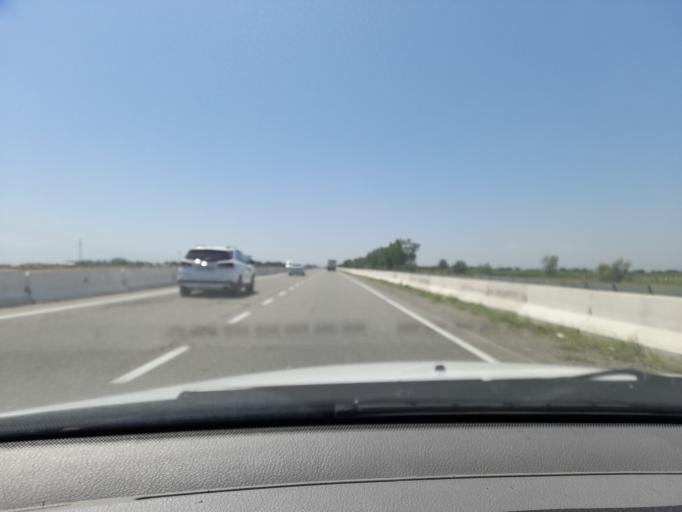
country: UZ
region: Jizzax
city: Paxtakor
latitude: 40.3378
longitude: 68.1157
